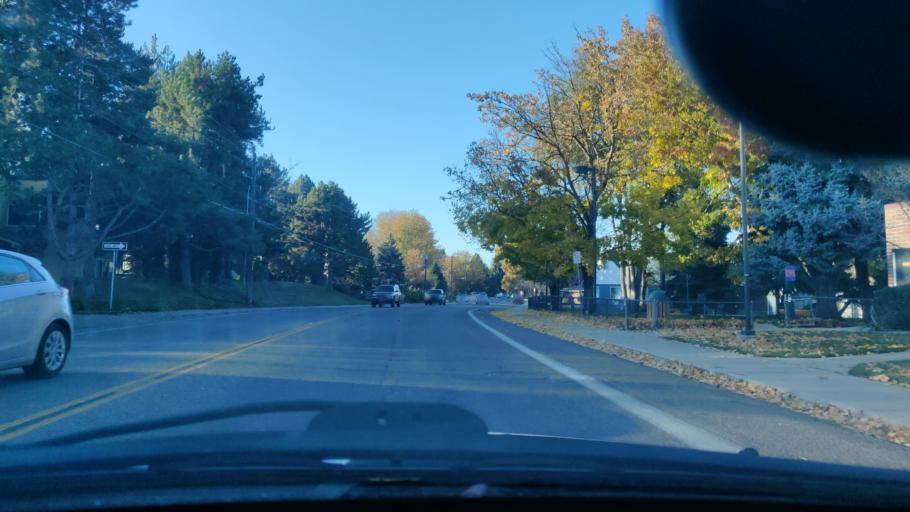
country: US
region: Idaho
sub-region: Ada County
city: Boise
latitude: 43.5989
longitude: -116.2061
